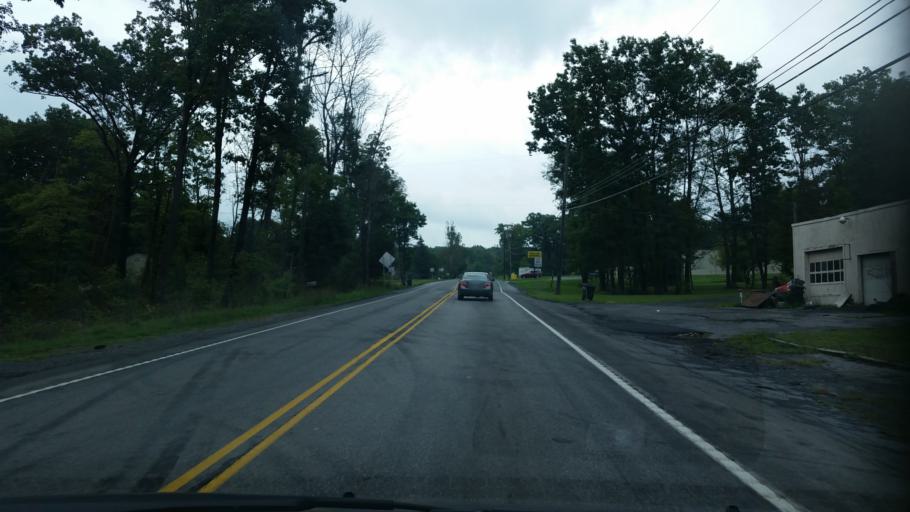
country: US
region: Pennsylvania
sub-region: Clearfield County
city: Shiloh
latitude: 40.9922
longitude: -78.3087
